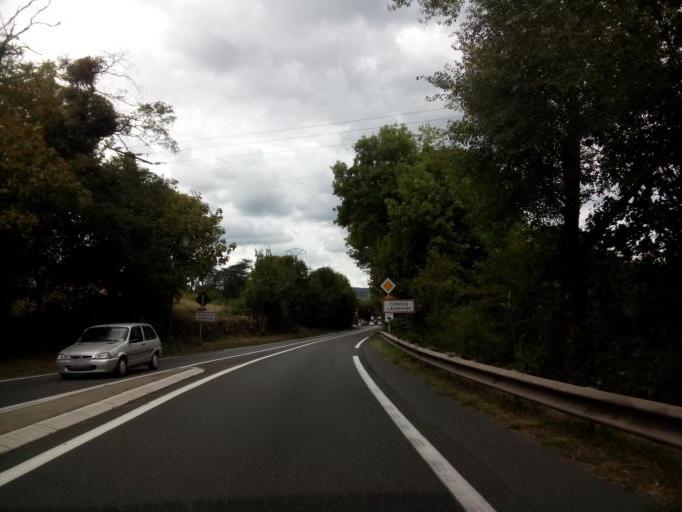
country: FR
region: Rhone-Alpes
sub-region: Departement du Rhone
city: Lozanne
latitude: 45.8553
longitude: 4.7163
